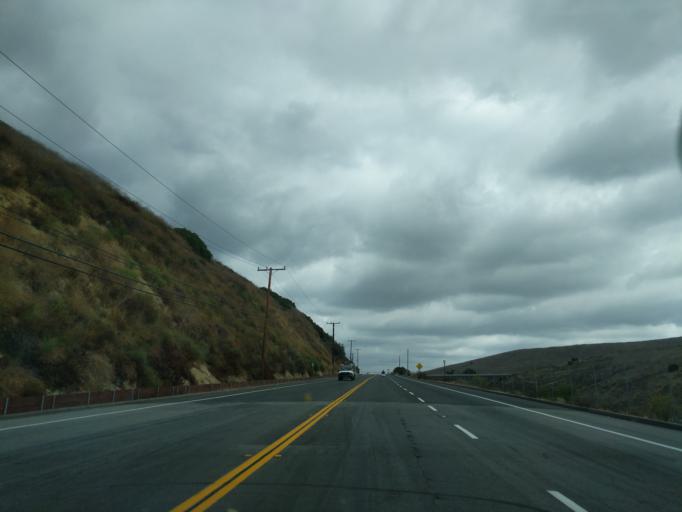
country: US
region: California
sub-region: Orange County
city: North Tustin
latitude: 33.7753
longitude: -117.7445
